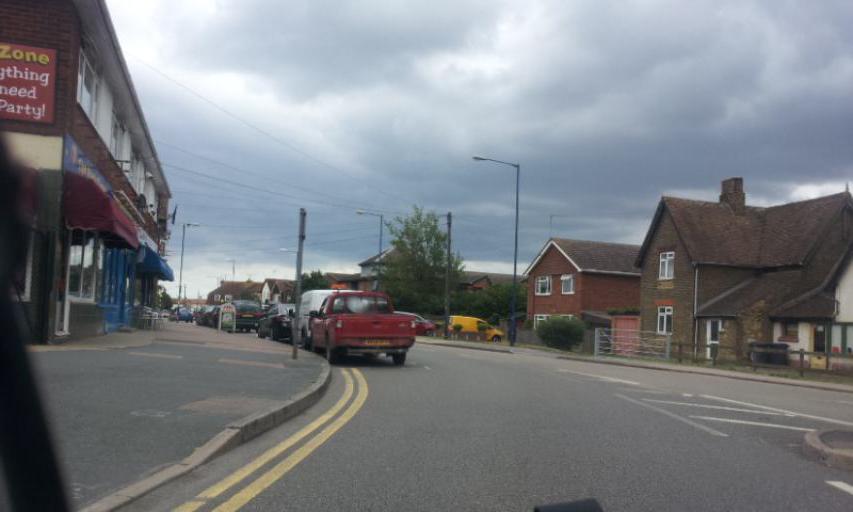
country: GB
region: England
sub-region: Kent
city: Tankerton
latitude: 51.3605
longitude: 1.0667
